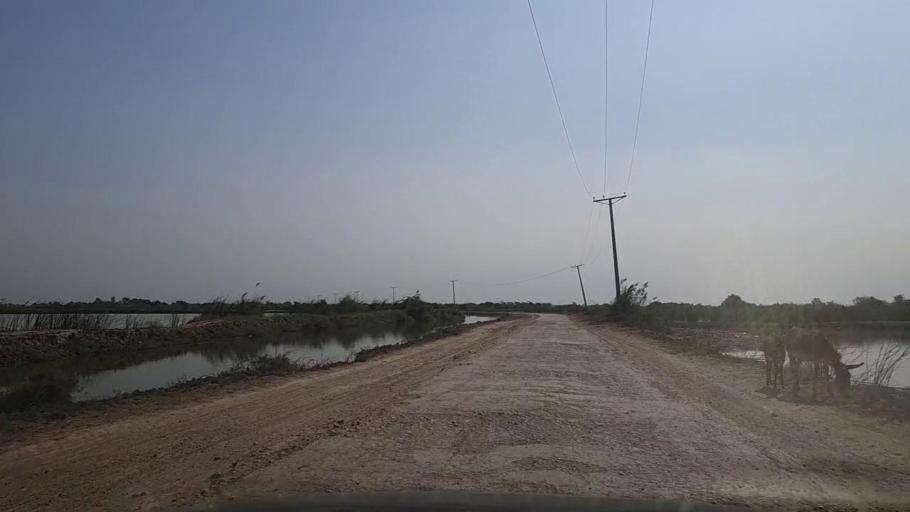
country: PK
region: Sindh
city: Thatta
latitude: 24.5849
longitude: 67.9084
